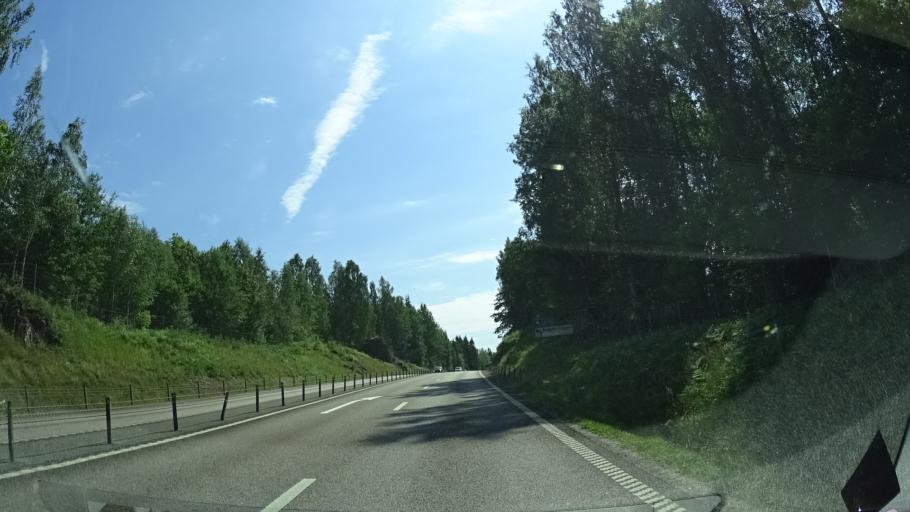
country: SE
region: Vaermland
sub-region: Kristinehamns Kommun
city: Kristinehamn
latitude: 59.3535
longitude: 14.0731
